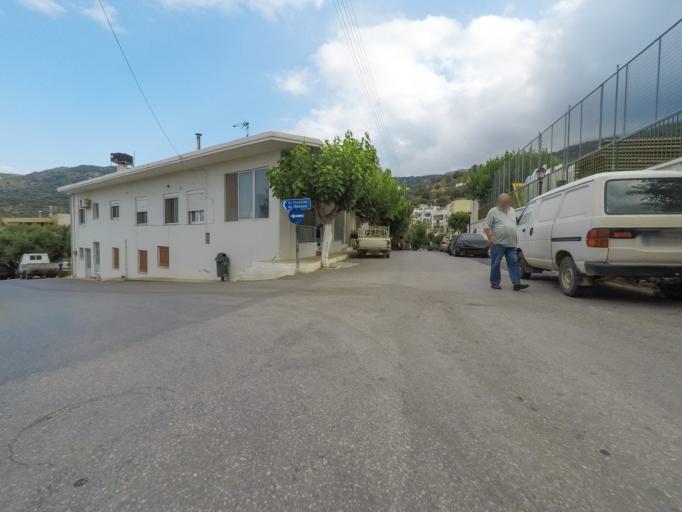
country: GR
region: Crete
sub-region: Nomos Lasithiou
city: Kritsa
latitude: 35.1560
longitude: 25.6468
